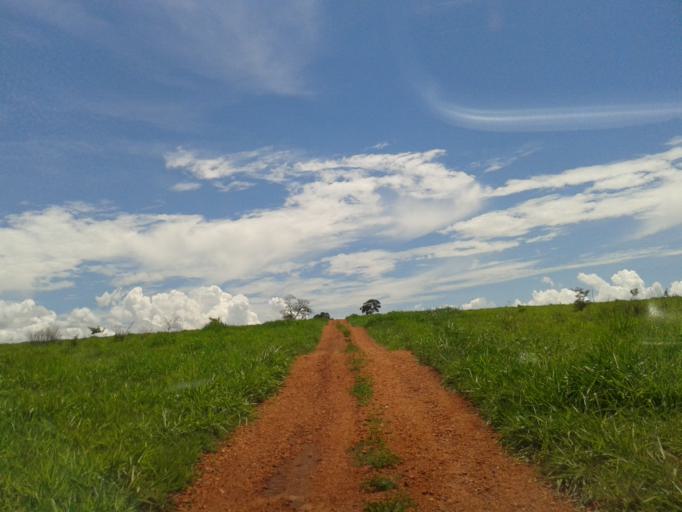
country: BR
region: Minas Gerais
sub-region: Santa Vitoria
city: Santa Vitoria
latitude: -19.1813
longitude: -50.6620
